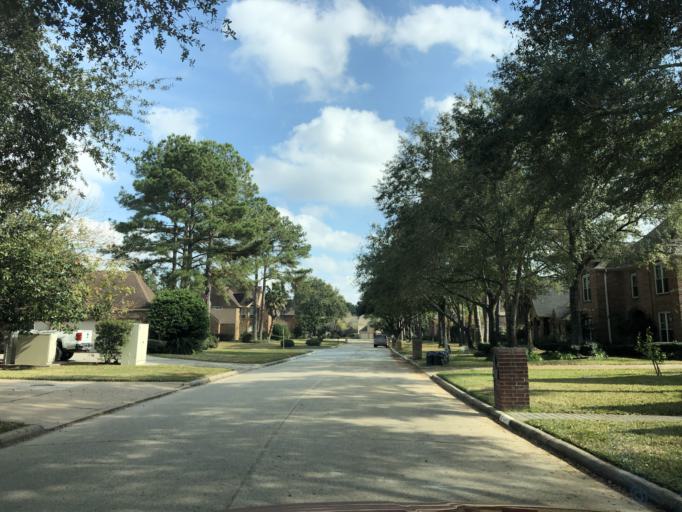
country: US
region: Texas
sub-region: Harris County
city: Tomball
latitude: 30.0223
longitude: -95.5464
